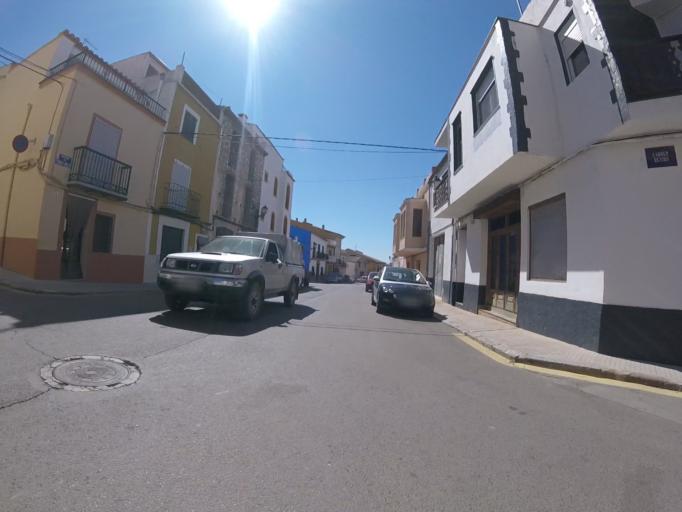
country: ES
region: Valencia
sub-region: Provincia de Castello
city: Chert/Xert
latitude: 40.4172
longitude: 0.1736
